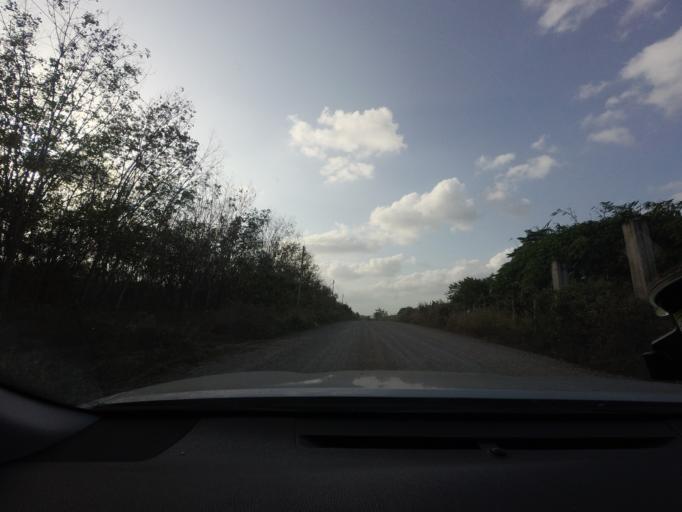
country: TH
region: Pattani
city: Mae Lan
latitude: 6.6165
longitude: 101.2553
